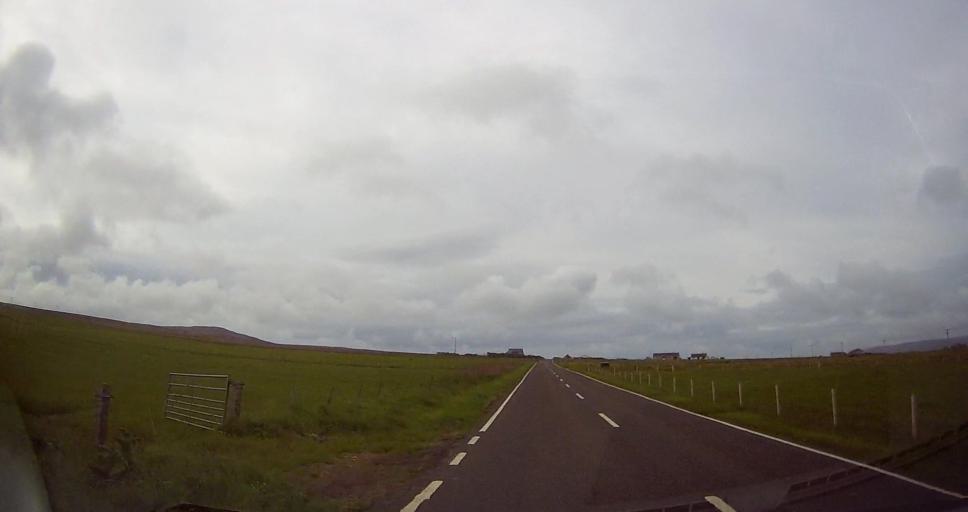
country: GB
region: Scotland
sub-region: Orkney Islands
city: Stromness
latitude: 58.9593
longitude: -3.2216
